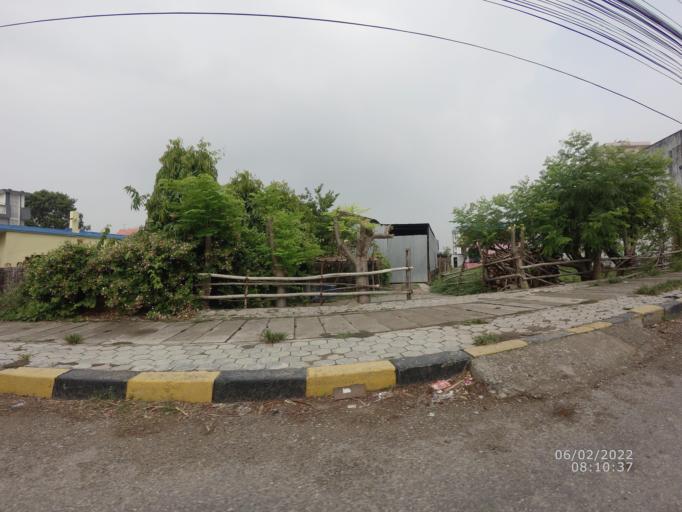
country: NP
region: Western Region
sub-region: Lumbini Zone
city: Bhairahawa
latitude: 27.4931
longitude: 83.4599
